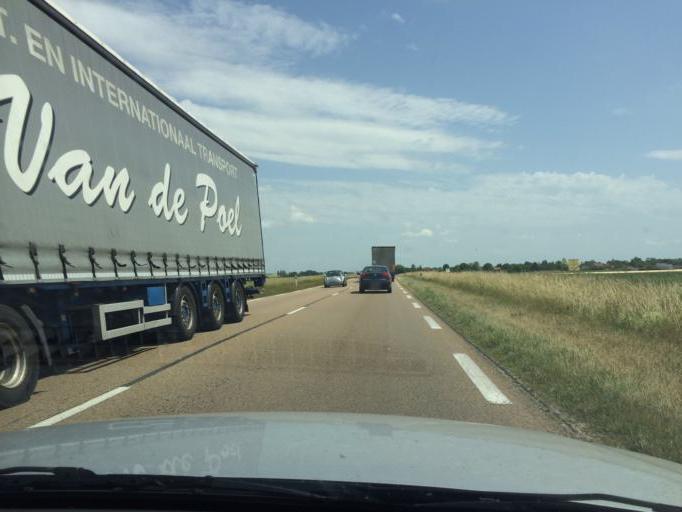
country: FR
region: Champagne-Ardenne
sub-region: Departement de la Marne
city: Sarry
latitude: 48.9172
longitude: 4.4224
